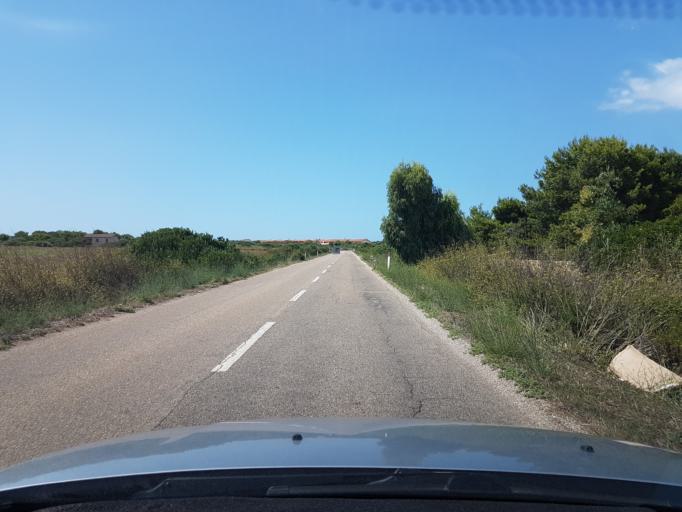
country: IT
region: Sardinia
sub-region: Provincia di Oristano
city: Riola Sardo
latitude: 40.0364
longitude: 8.4204
